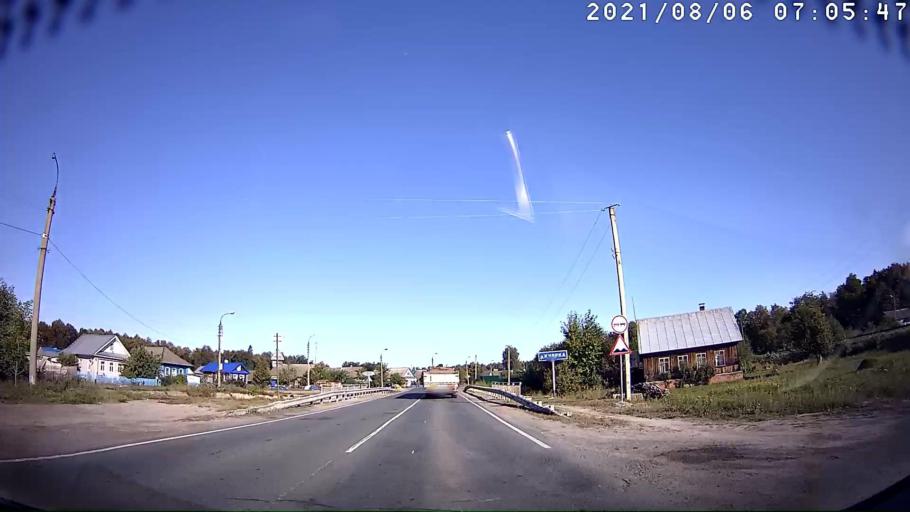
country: RU
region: Mariy-El
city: Yoshkar-Ola
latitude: 56.5554
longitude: 47.9852
